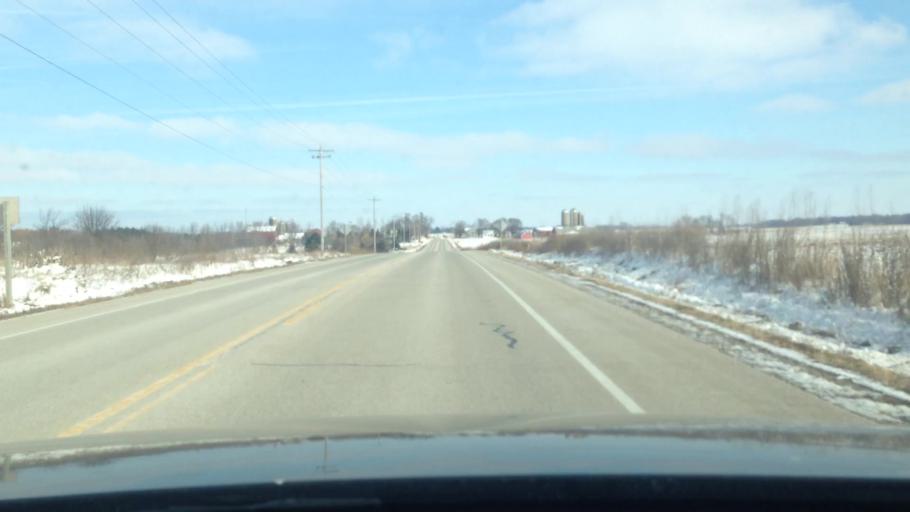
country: US
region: Wisconsin
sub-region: Walworth County
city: Lake Geneva
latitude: 42.6701
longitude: -88.4130
